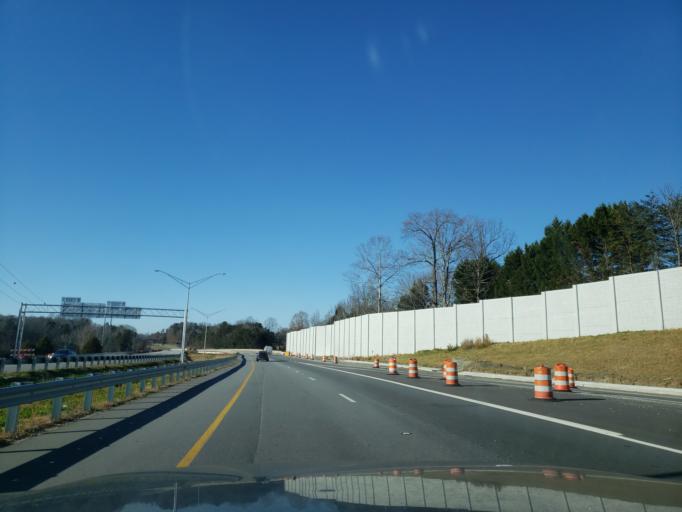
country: US
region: North Carolina
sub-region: Guilford County
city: High Point
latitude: 36.0037
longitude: -79.9938
